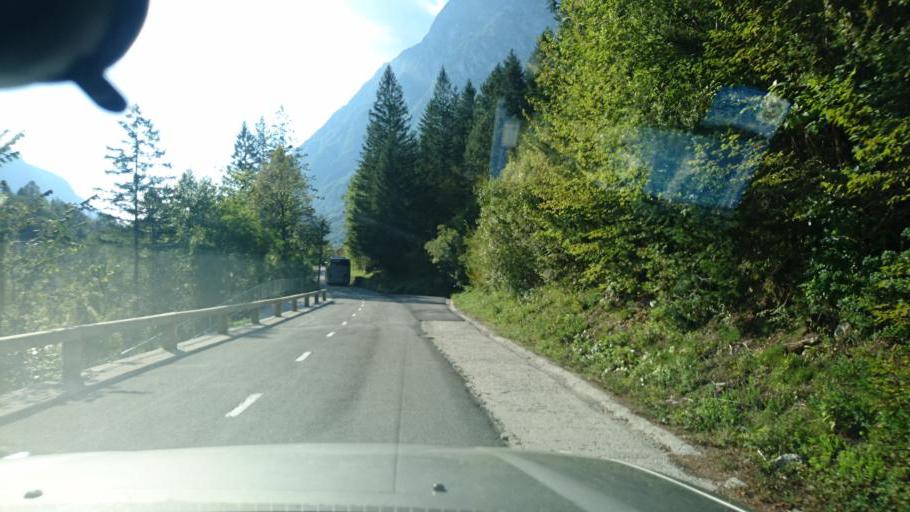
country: SI
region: Bovec
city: Bovec
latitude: 46.3416
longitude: 13.6756
